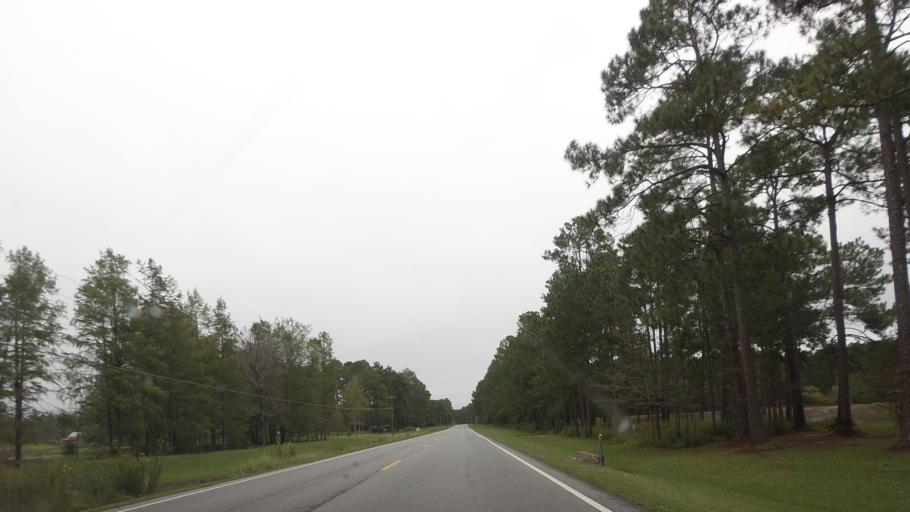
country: US
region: Georgia
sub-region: Berrien County
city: Nashville
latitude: 31.2482
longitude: -83.2420
